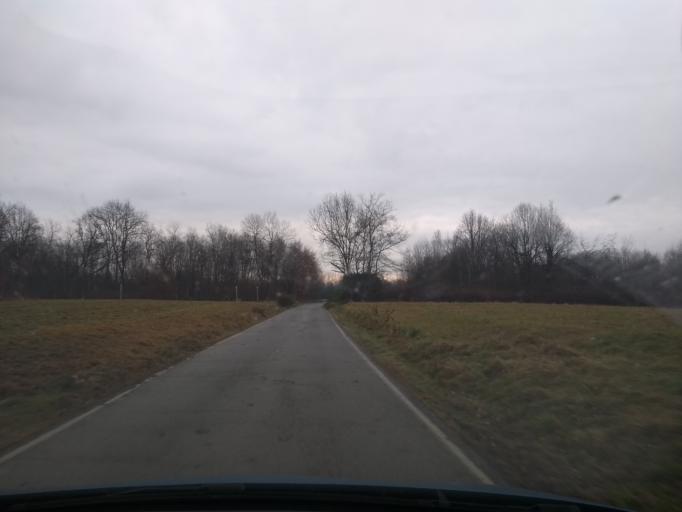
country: IT
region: Piedmont
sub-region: Provincia di Torino
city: Front
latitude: 45.2764
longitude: 7.6458
